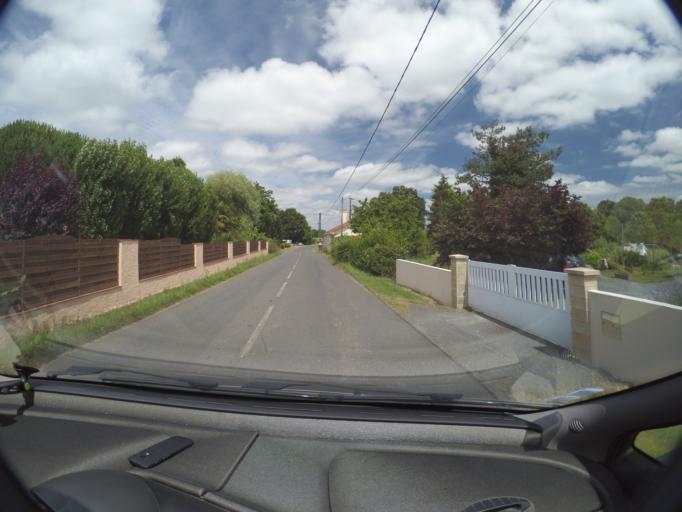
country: FR
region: Pays de la Loire
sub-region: Departement de la Loire-Atlantique
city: Gorges
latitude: 47.1160
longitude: -1.2913
